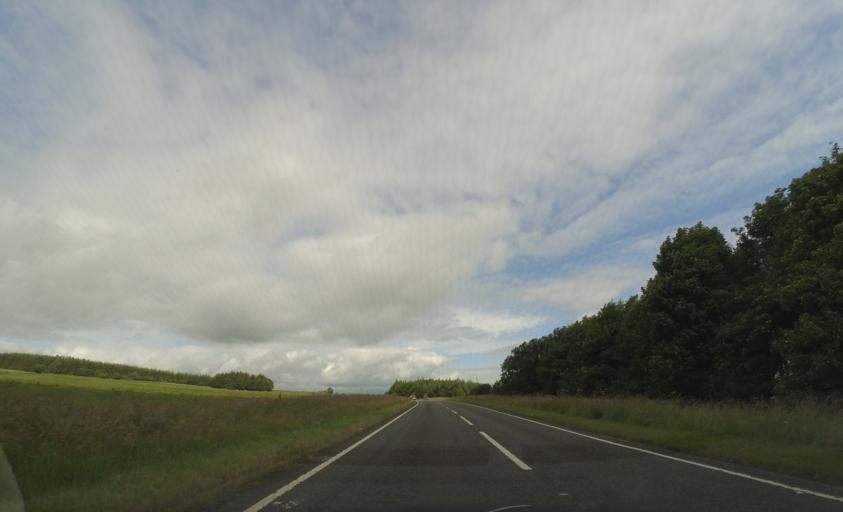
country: GB
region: Scotland
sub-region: The Scottish Borders
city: Hawick
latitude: 55.4691
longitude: -2.7918
